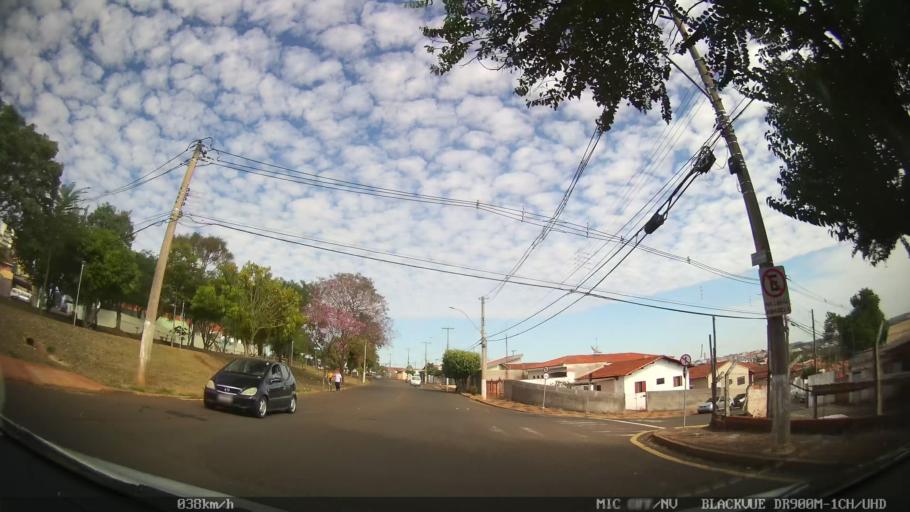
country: BR
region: Sao Paulo
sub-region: Santa Barbara D'Oeste
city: Santa Barbara d'Oeste
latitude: -22.7609
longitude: -47.4051
